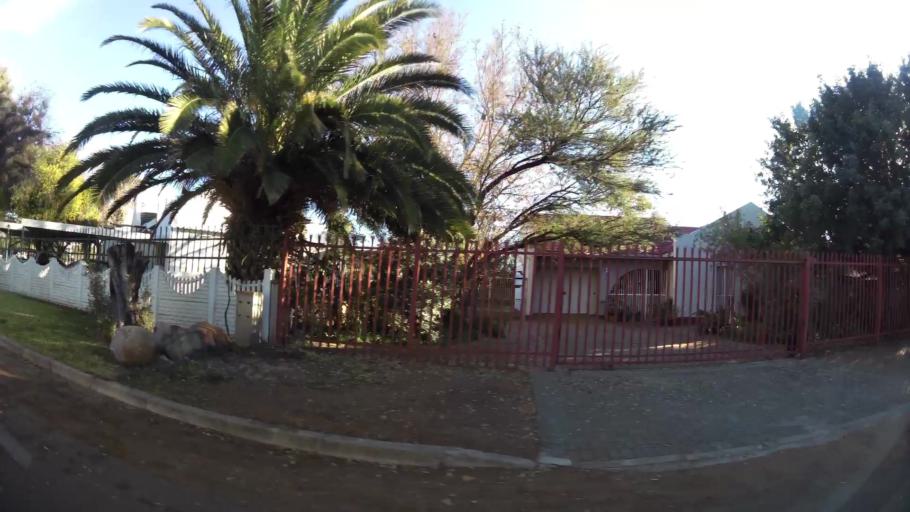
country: ZA
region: Northern Cape
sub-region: Frances Baard District Municipality
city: Kimberley
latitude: -28.7466
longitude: 24.7248
